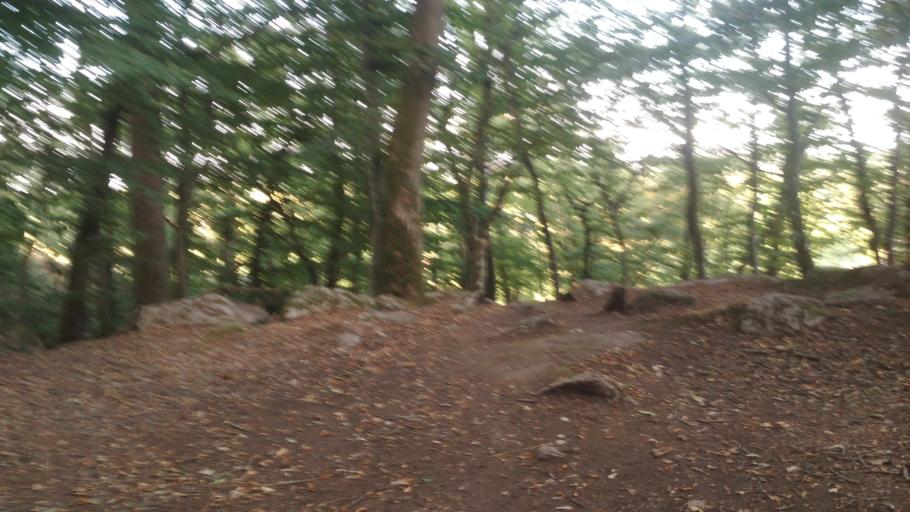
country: DK
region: Capital Region
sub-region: Bornholm Kommune
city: Akirkeby
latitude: 55.1115
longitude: 14.9034
